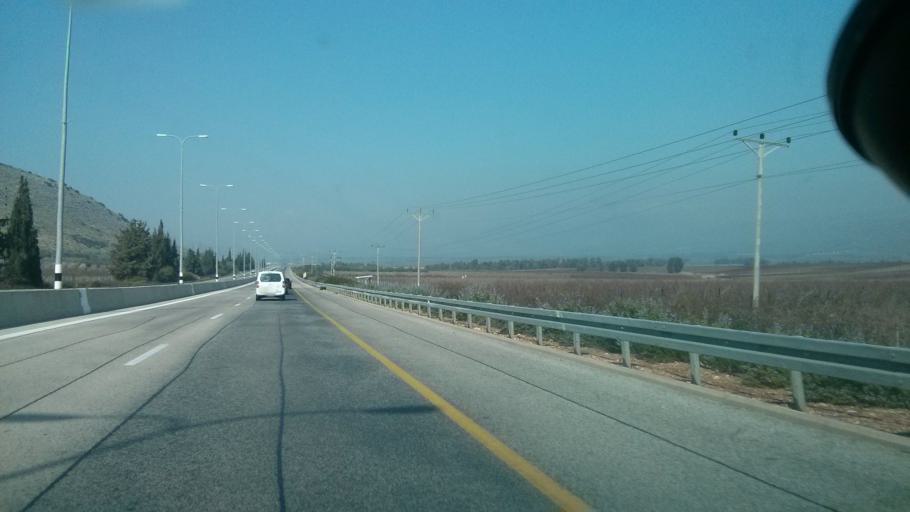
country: IL
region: Northern District
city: Rosh Pinna
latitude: 33.0590
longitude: 35.5742
